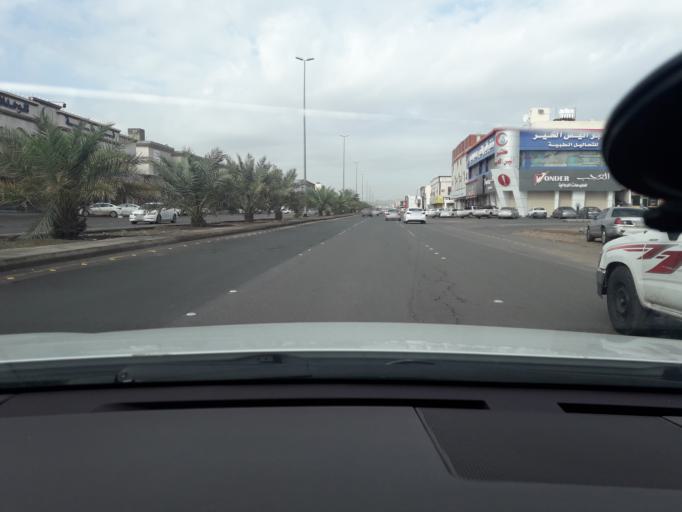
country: SA
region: Al Madinah al Munawwarah
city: Sultanah
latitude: 24.4504
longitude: 39.5159
